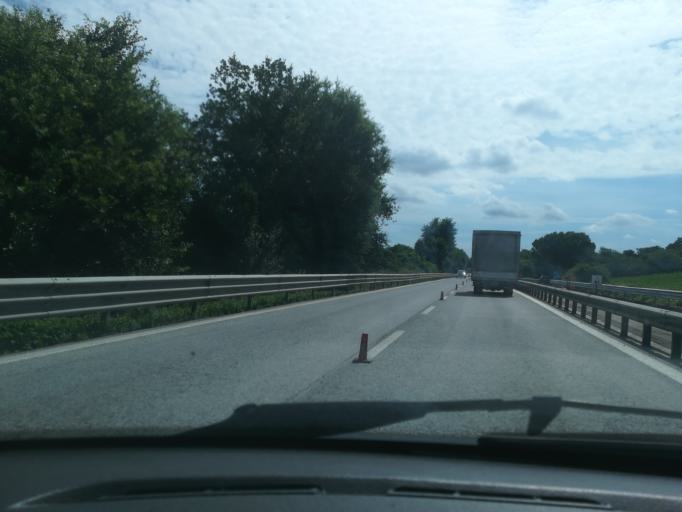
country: IT
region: The Marches
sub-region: Provincia di Macerata
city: Zona Industriale
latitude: 43.2692
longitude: 13.5080
